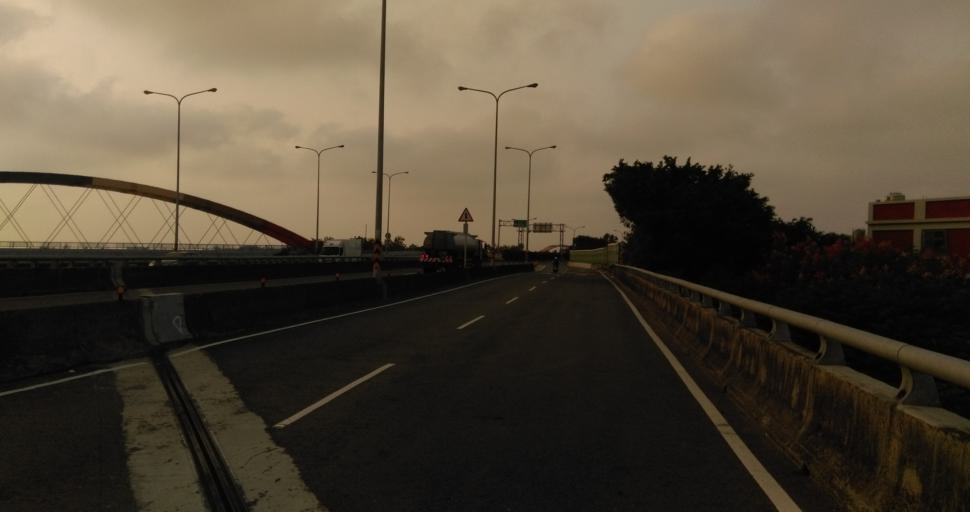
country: TW
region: Taiwan
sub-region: Hsinchu
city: Hsinchu
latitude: 24.8055
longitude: 120.9192
